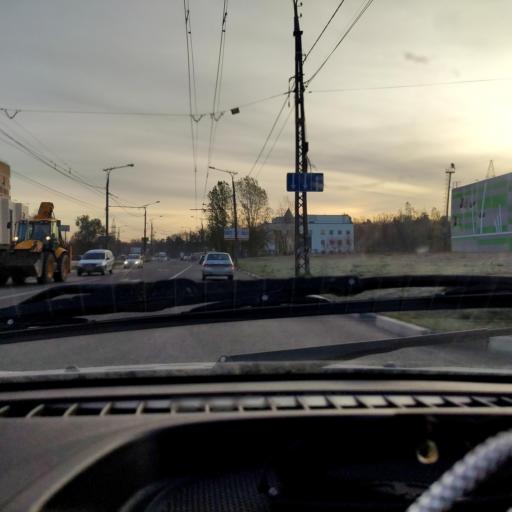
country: RU
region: Samara
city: Tol'yatti
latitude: 53.5008
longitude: 49.4214
